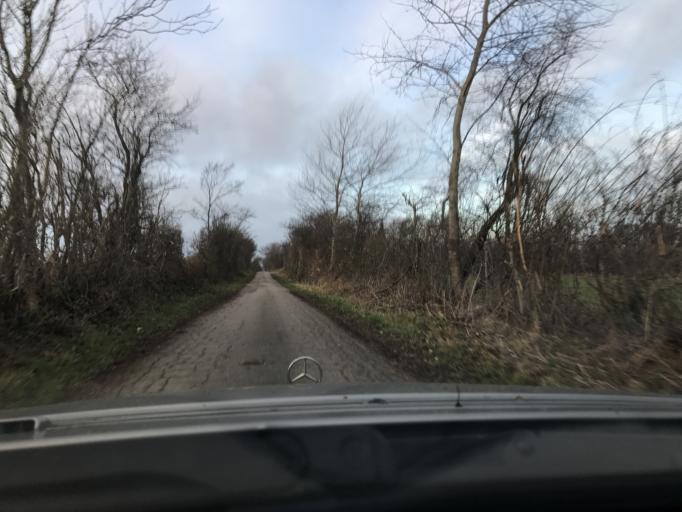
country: DK
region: South Denmark
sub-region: Sonderborg Kommune
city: Nordborg
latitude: 55.0560
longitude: 9.6725
